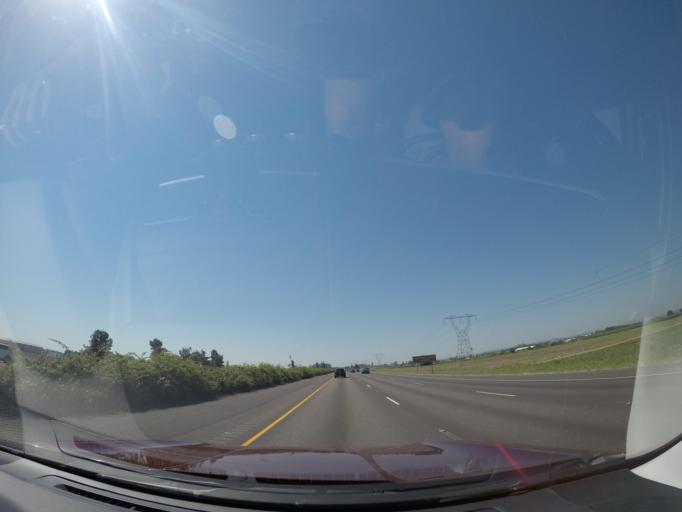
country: US
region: Oregon
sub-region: Marion County
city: Hayesville
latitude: 45.0584
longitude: -122.9681
